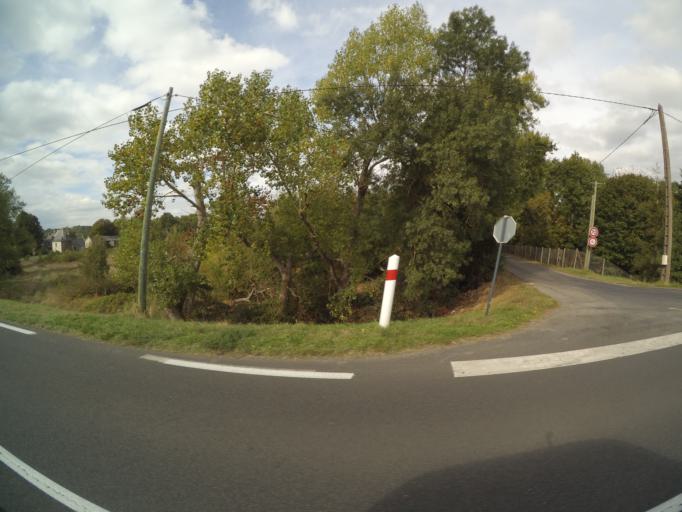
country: FR
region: Centre
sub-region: Departement d'Indre-et-Loire
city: Saint-Etienne-de-Chigny
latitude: 47.3717
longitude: 0.5434
